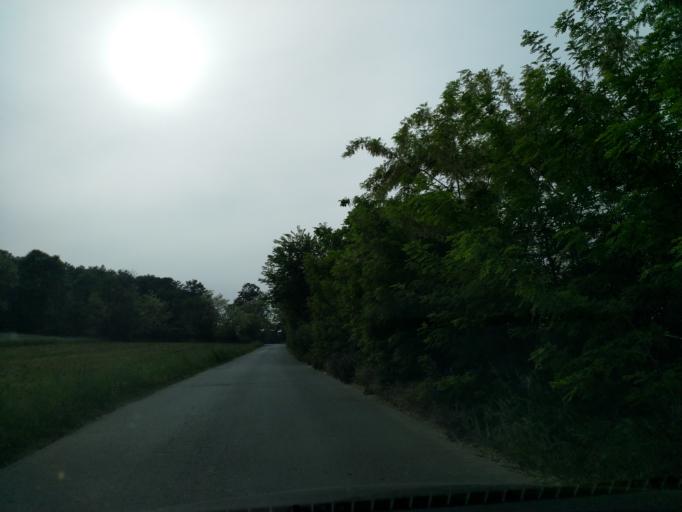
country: RS
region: Central Serbia
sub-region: Pomoravski Okrug
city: Jagodina
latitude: 43.9739
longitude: 21.2111
